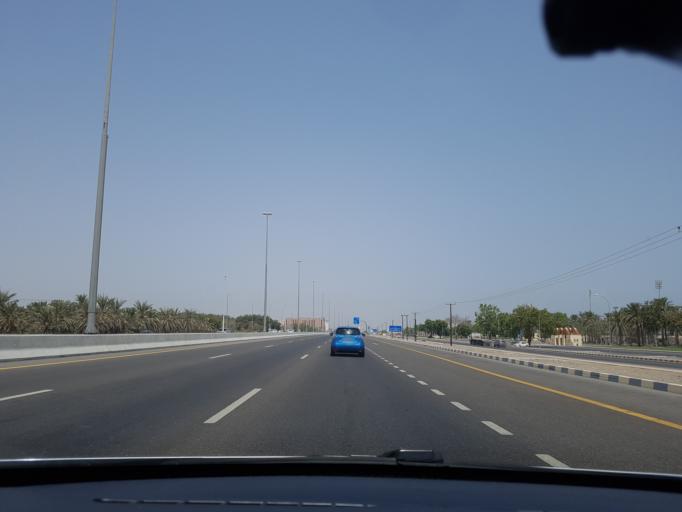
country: OM
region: Al Batinah
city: Al Sohar
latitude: 24.3305
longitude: 56.7412
